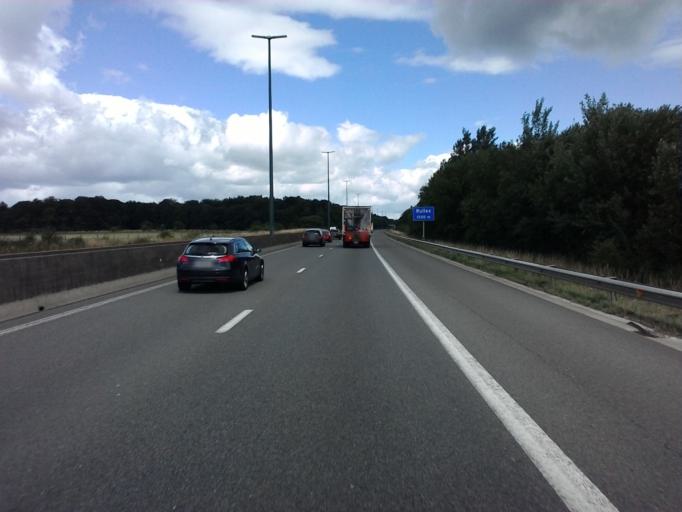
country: BE
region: Wallonia
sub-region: Province du Luxembourg
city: Habay-la-Vieille
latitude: 49.7294
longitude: 5.5812
